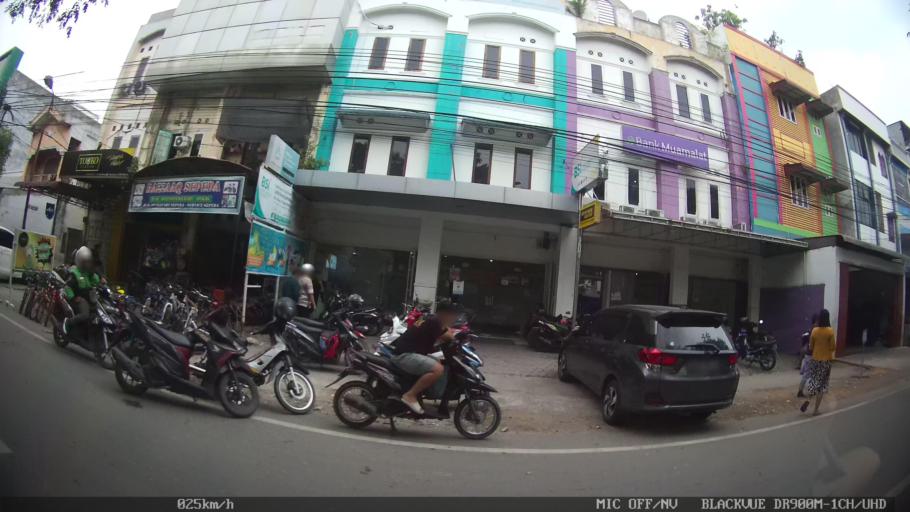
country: ID
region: North Sumatra
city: Medan
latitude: 3.5783
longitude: 98.7031
